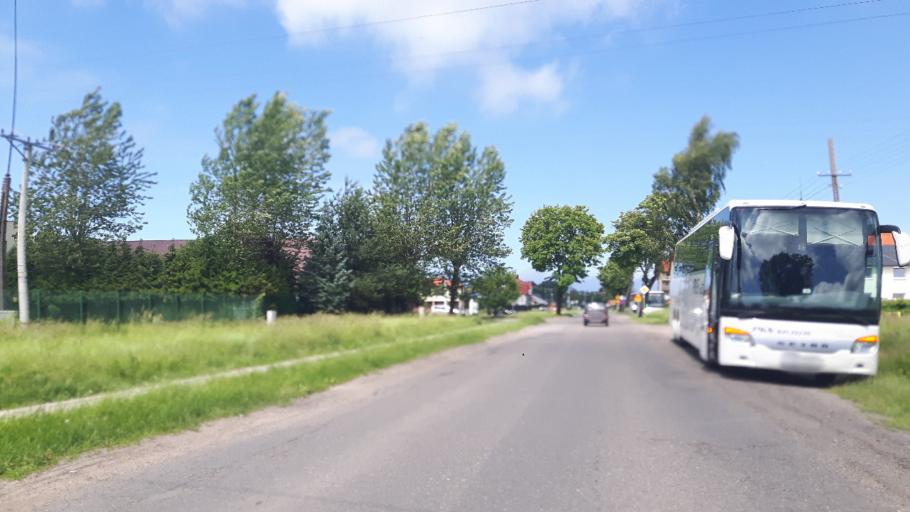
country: PL
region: Pomeranian Voivodeship
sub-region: Powiat slupski
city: Ustka
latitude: 54.5714
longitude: 16.8512
